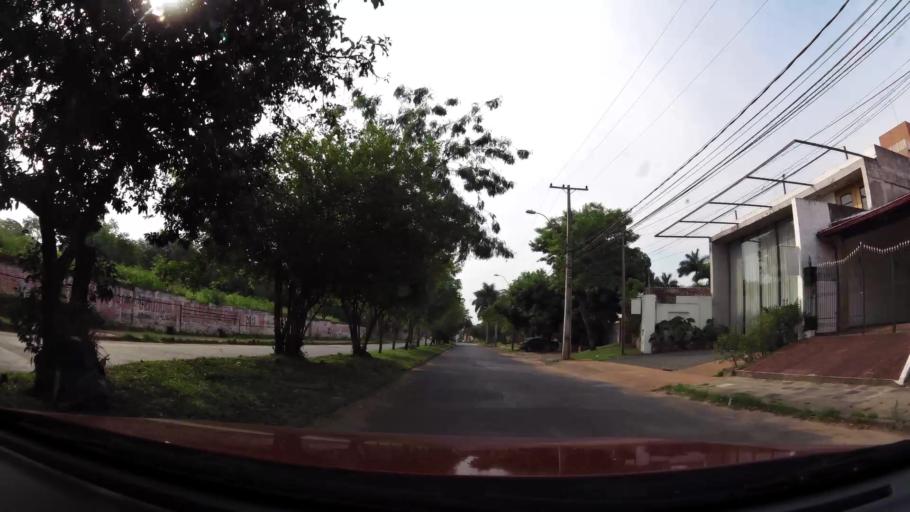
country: PY
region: Asuncion
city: Asuncion
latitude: -25.2719
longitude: -57.5711
